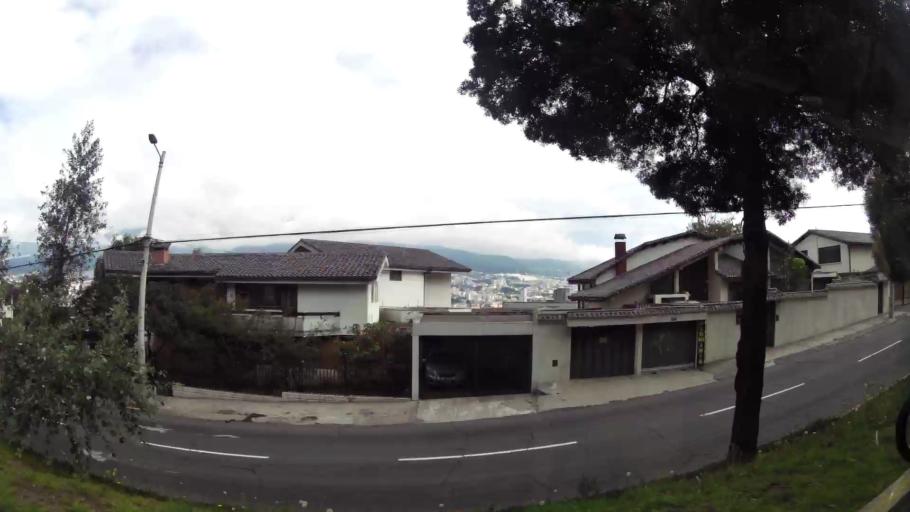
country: EC
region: Pichincha
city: Quito
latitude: -0.1744
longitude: -78.4719
